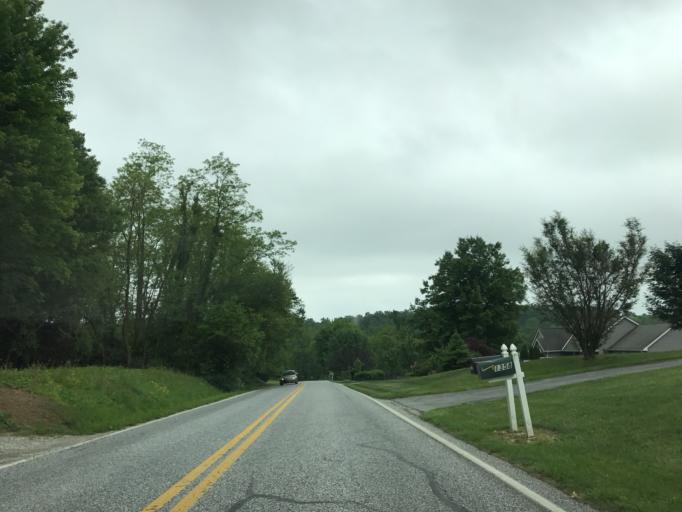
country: US
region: Pennsylvania
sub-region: York County
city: Susquehanna Trails
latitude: 39.7624
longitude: -76.4643
